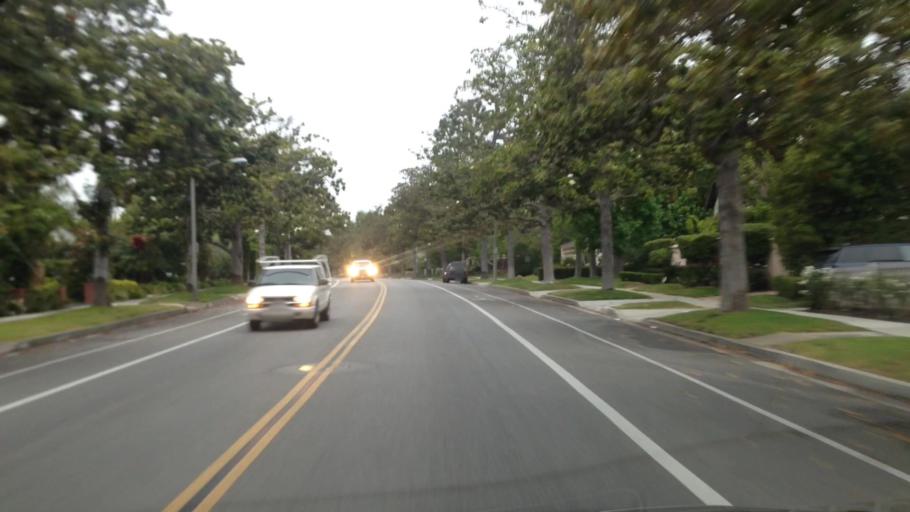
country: US
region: California
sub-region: Los Angeles County
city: Beverly Hills
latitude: 34.0796
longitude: -118.4073
